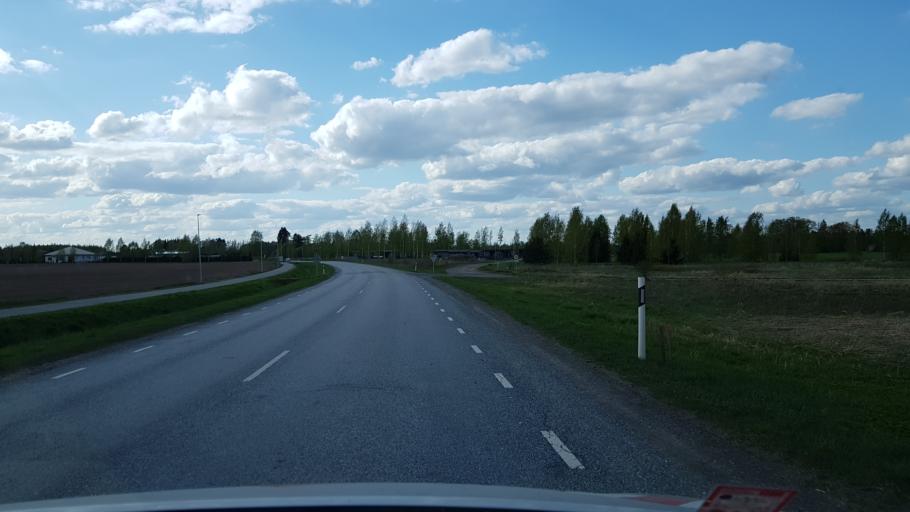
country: EE
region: Tartu
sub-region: UElenurme vald
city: Ulenurme
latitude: 58.3205
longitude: 26.8300
